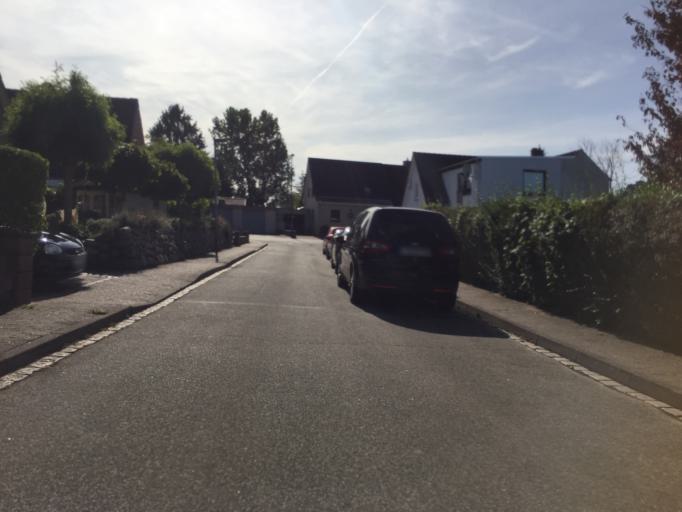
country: DE
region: Schleswig-Holstein
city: Itzehoe
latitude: 53.9084
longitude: 9.4966
